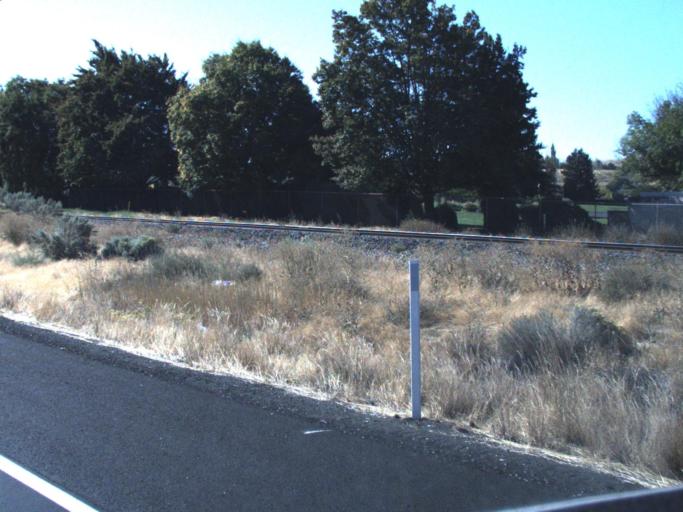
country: US
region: Washington
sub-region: Benton County
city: Richland
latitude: 46.2814
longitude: -119.3067
